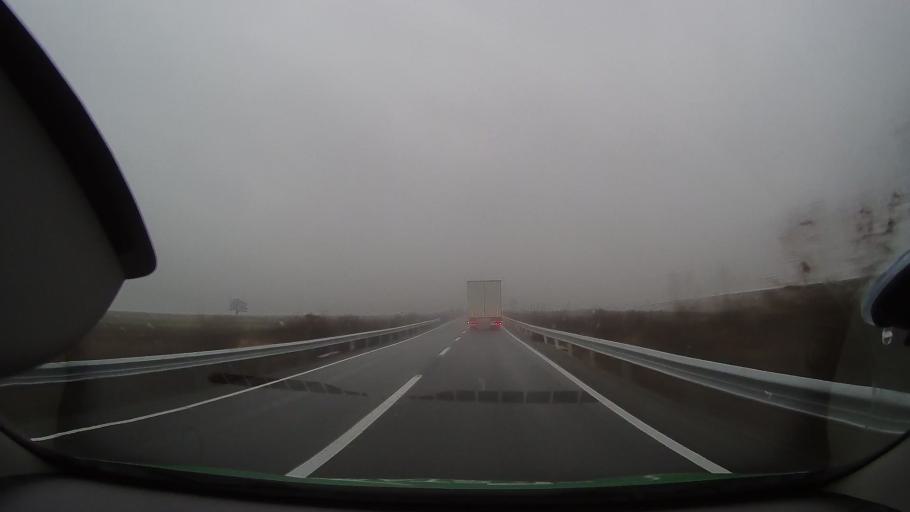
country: RO
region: Bihor
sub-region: Comuna Olcea
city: Olcea
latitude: 46.6659
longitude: 21.9634
